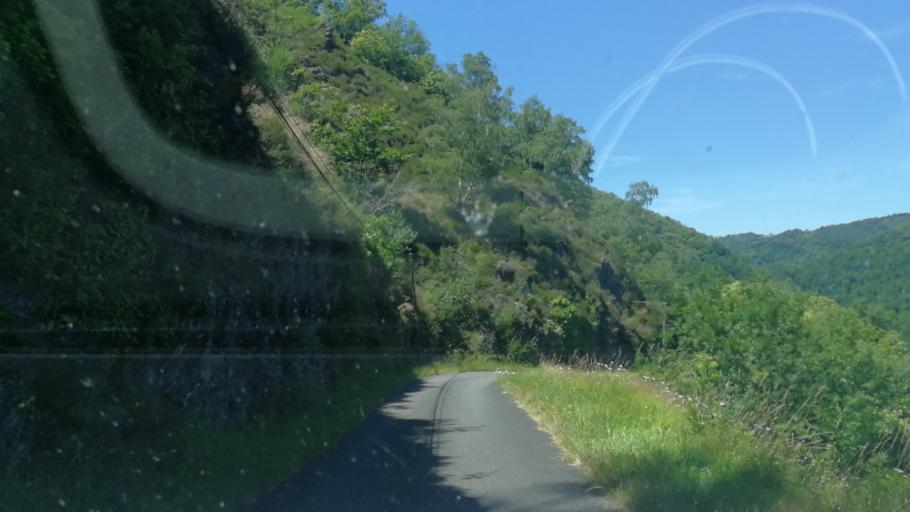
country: FR
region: Midi-Pyrenees
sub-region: Departement de l'Aveyron
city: Firmi
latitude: 44.5957
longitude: 2.3914
